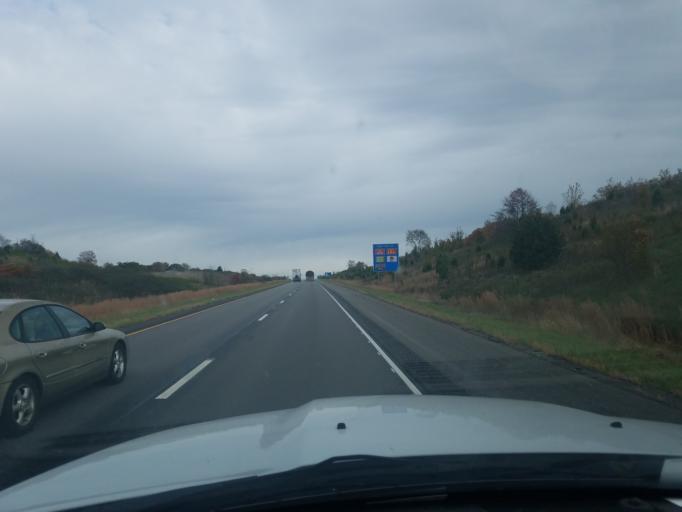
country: US
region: Indiana
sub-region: Dubois County
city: Ferdinand
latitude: 38.2037
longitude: -86.8994
